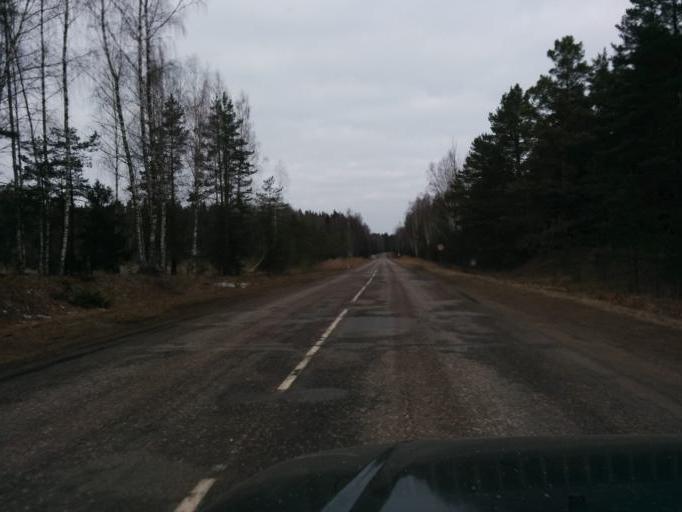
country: LV
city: Tireli
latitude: 56.8754
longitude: 23.5399
